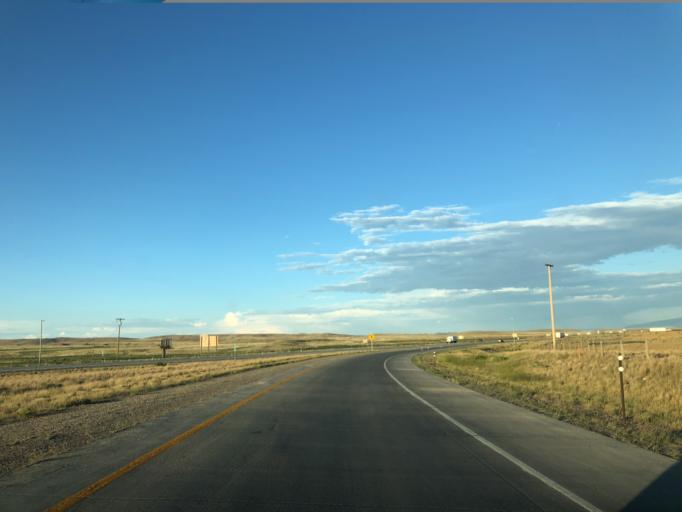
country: US
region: Wyoming
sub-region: Carbon County
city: Rawlins
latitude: 41.7878
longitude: -107.1940
